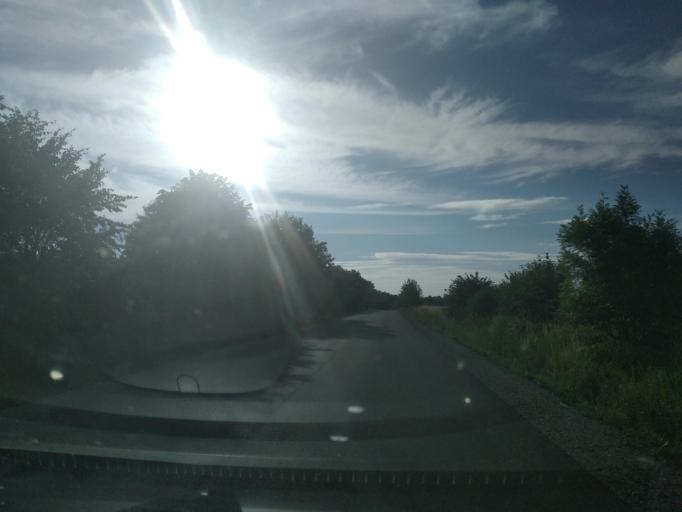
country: PL
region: Subcarpathian Voivodeship
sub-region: Powiat sanocki
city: Strachocina
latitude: 49.5757
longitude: 22.1263
